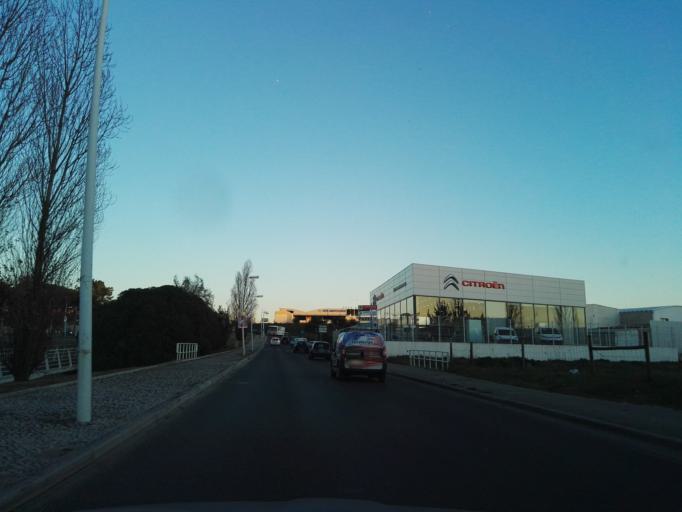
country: PT
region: Setubal
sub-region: Seixal
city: Corroios
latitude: 38.6338
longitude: -9.1436
